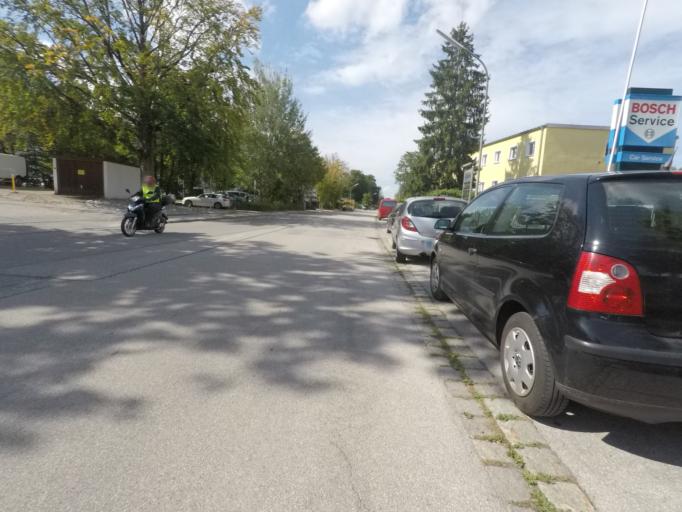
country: DE
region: Bavaria
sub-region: Upper Bavaria
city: Geretsried
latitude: 47.8498
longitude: 11.4946
